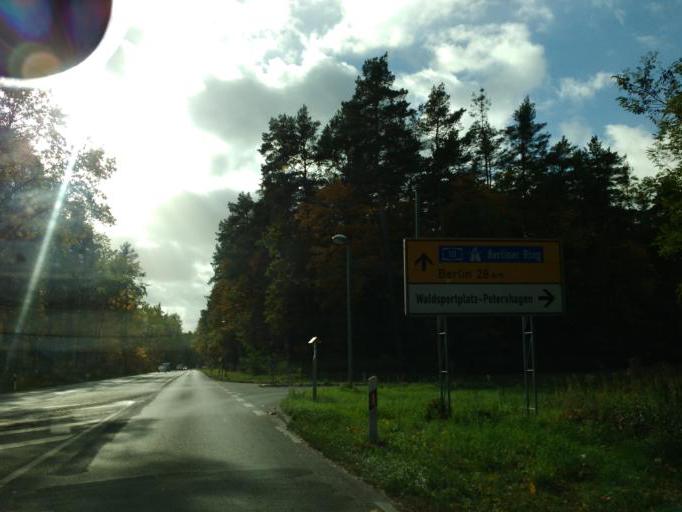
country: DE
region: Brandenburg
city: Petershagen
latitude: 52.5174
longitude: 13.8085
